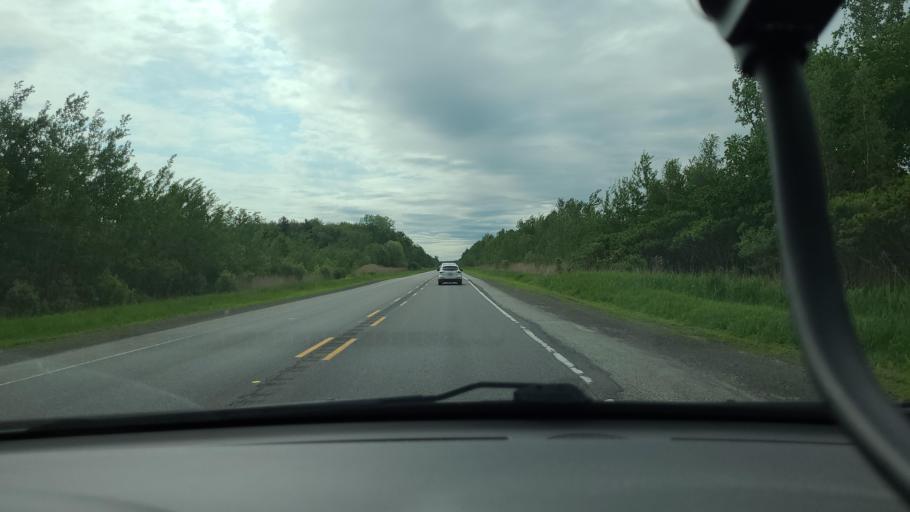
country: CA
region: Quebec
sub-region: Lanaudiere
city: Saint-Jacques
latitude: 45.9695
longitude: -73.5329
